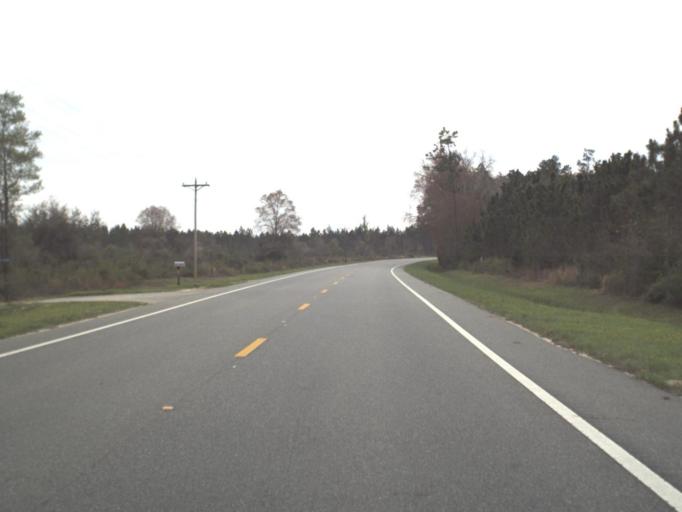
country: US
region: Florida
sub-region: Gulf County
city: Wewahitchka
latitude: 30.2589
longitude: -85.2357
